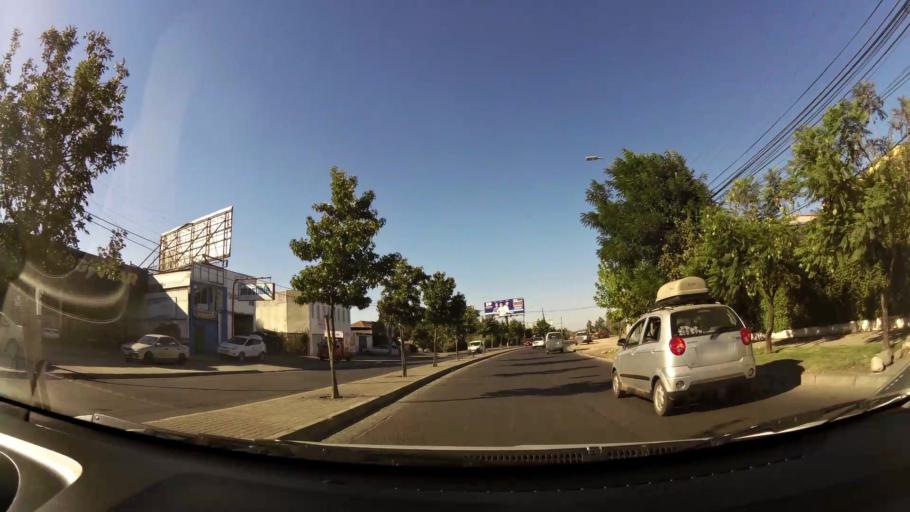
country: CL
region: O'Higgins
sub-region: Provincia de Colchagua
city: Chimbarongo
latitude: -34.5835
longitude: -70.9837
